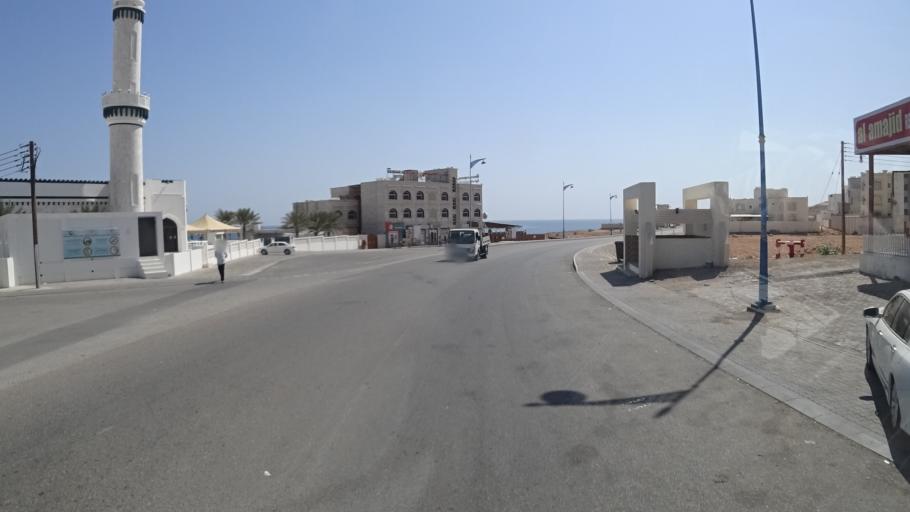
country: OM
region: Ash Sharqiyah
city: Sur
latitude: 22.5668
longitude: 59.5531
